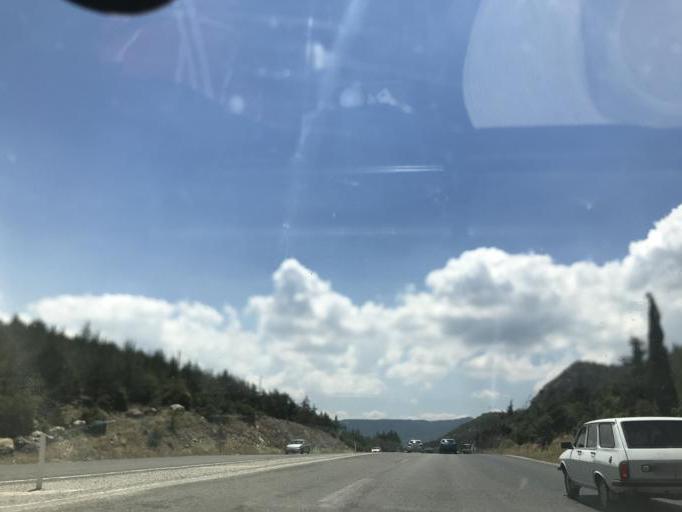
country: TR
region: Denizli
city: Honaz
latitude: 37.7048
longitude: 29.2036
